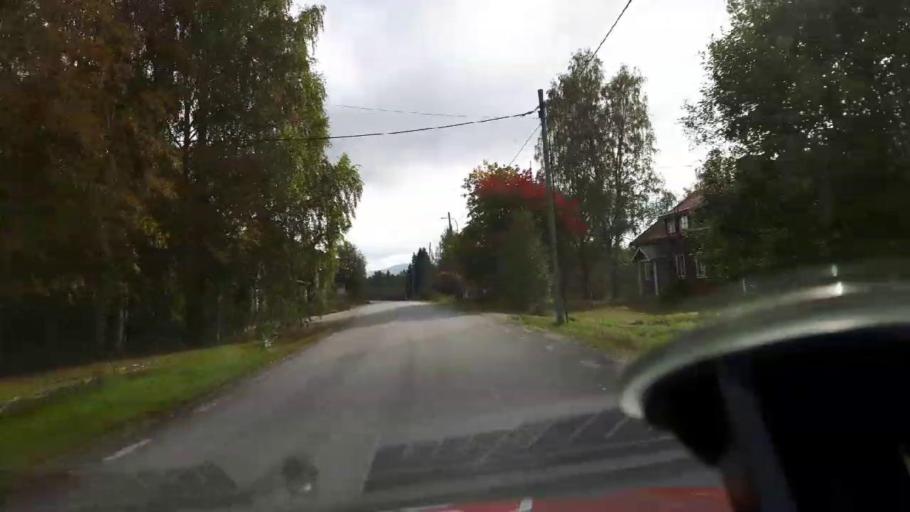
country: SE
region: Gaevleborg
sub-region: Ljusdals Kommun
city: Farila
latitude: 61.7877
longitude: 15.9210
